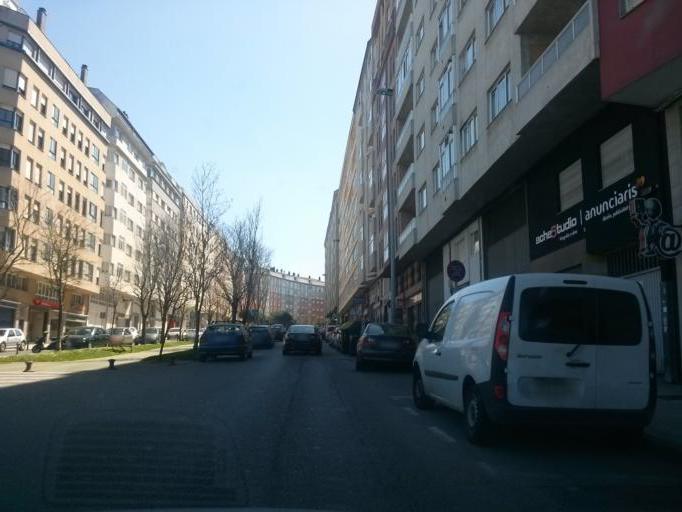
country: ES
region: Galicia
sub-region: Provincia de Lugo
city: Lugo
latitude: 43.0037
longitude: -7.5459
